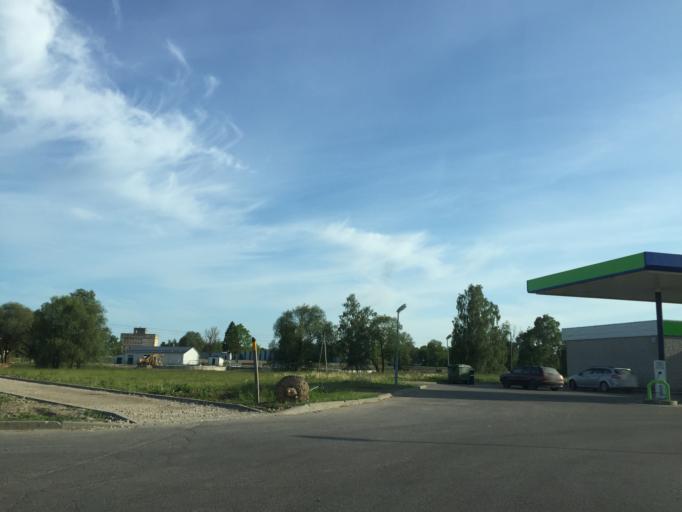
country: LV
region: Bauskas Rajons
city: Bauska
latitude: 56.3996
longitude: 24.1779
